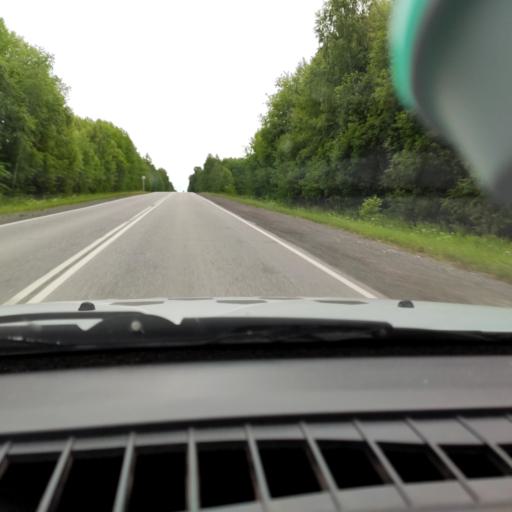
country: RU
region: Perm
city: Lys'va
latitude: 58.1453
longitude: 57.7515
